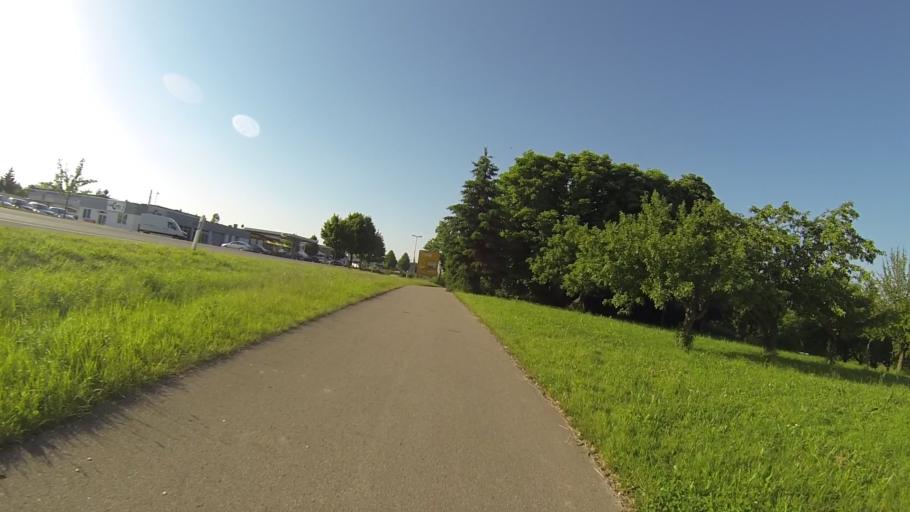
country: DE
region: Baden-Wuerttemberg
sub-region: Tuebingen Region
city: Laupheim
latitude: 48.2178
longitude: 9.8790
